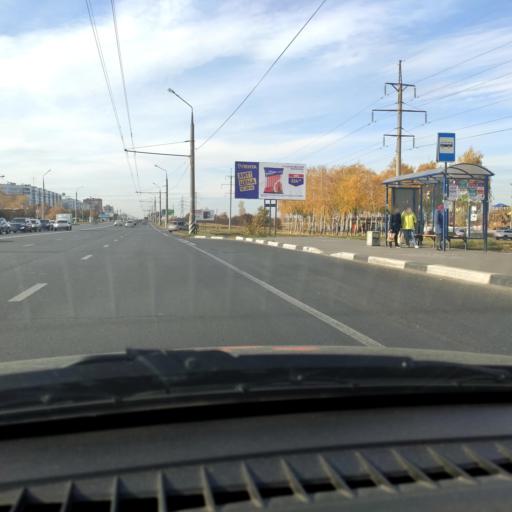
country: RU
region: Samara
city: Tol'yatti
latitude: 53.5470
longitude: 49.3607
